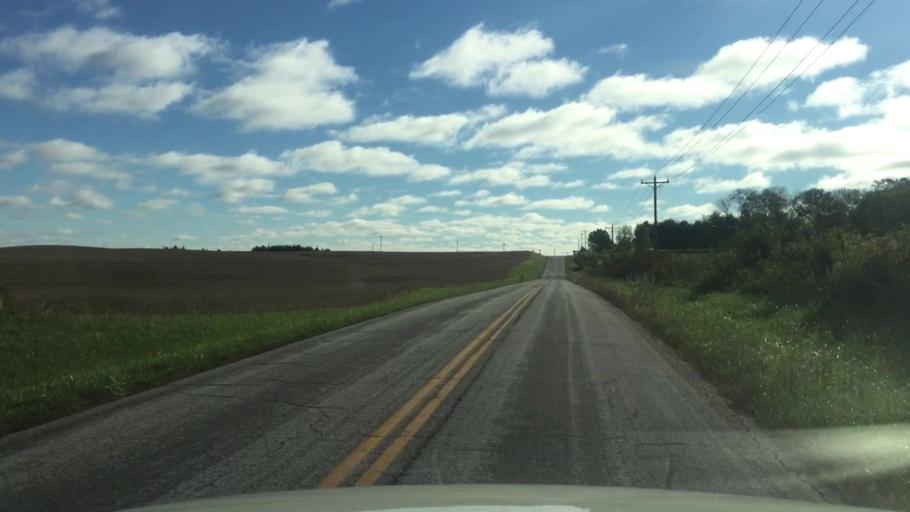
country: US
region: Missouri
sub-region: Howard County
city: Fayette
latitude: 39.1044
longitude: -92.7396
